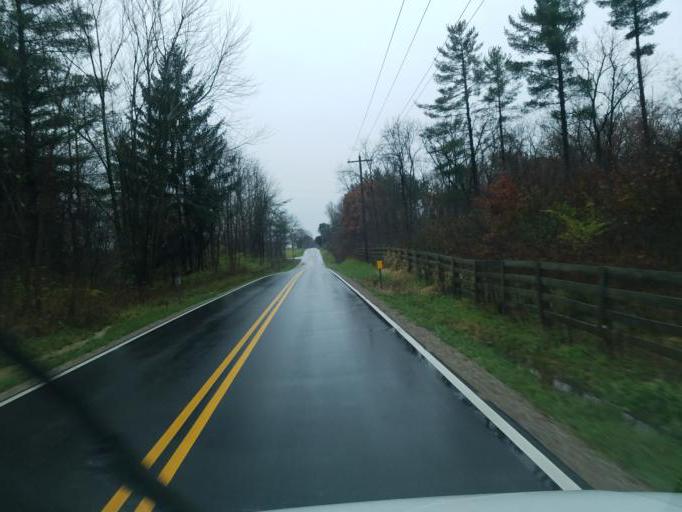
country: US
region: Ohio
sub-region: Delaware County
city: Ashley
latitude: 40.3514
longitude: -82.9217
